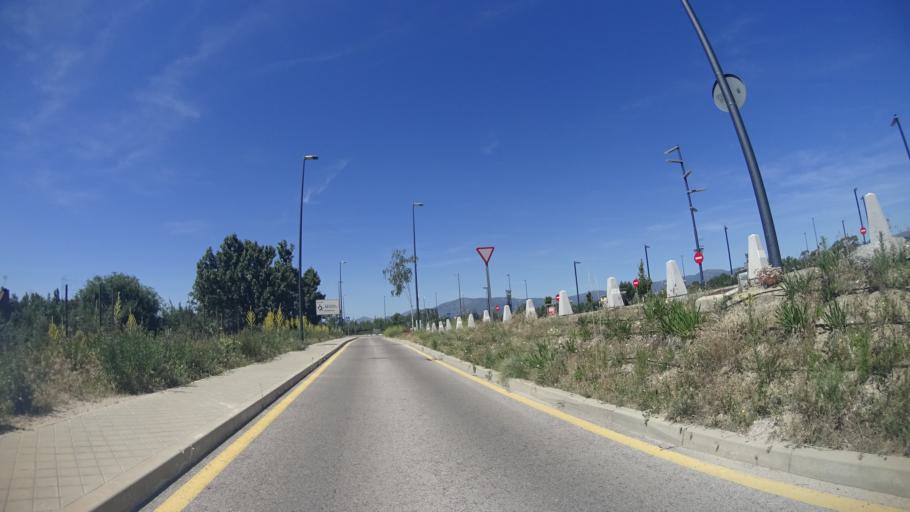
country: ES
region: Madrid
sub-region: Provincia de Madrid
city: Collado-Villalba
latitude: 40.6531
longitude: -4.0017
